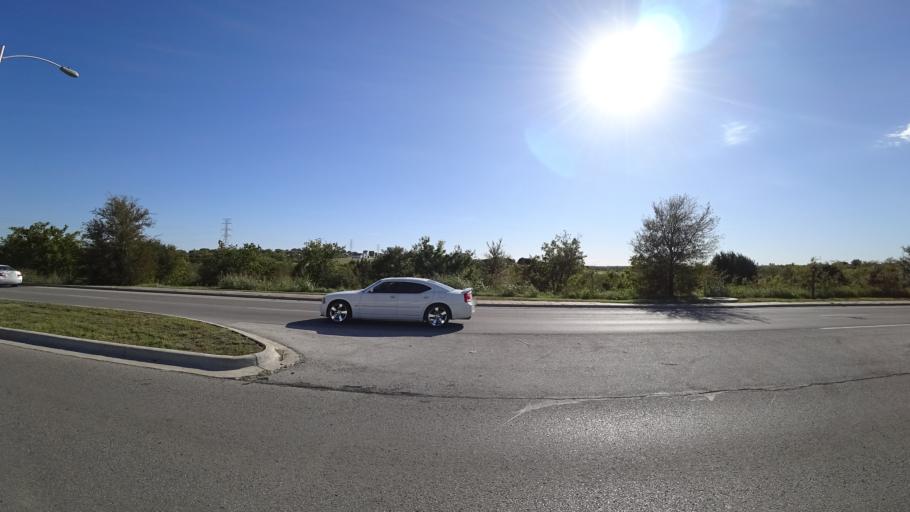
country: US
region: Texas
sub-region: Travis County
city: Hornsby Bend
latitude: 30.2970
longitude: -97.6396
